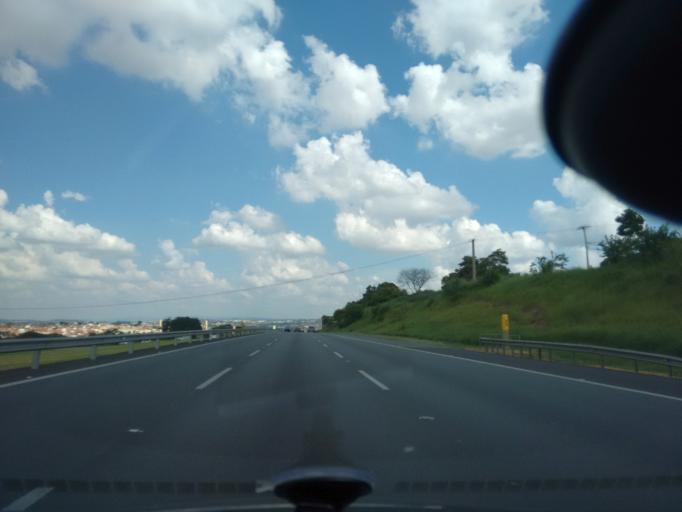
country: BR
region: Sao Paulo
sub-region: Campinas
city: Campinas
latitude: -22.9340
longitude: -47.1279
